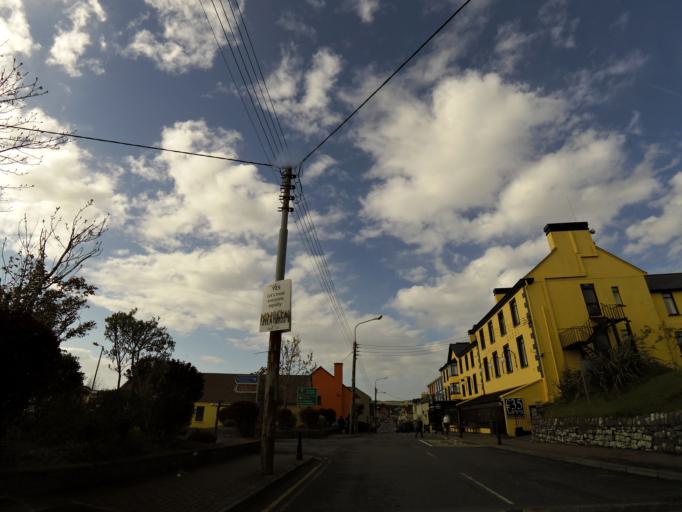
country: IE
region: Connaught
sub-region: County Galway
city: Bearna
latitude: 53.0279
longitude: -9.2899
